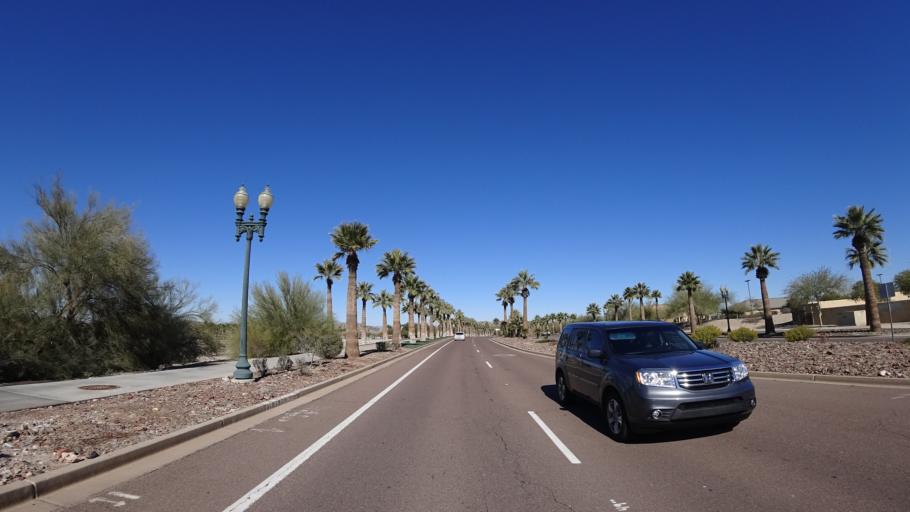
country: US
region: Arizona
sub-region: Maricopa County
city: Goodyear
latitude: 33.3503
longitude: -112.4285
